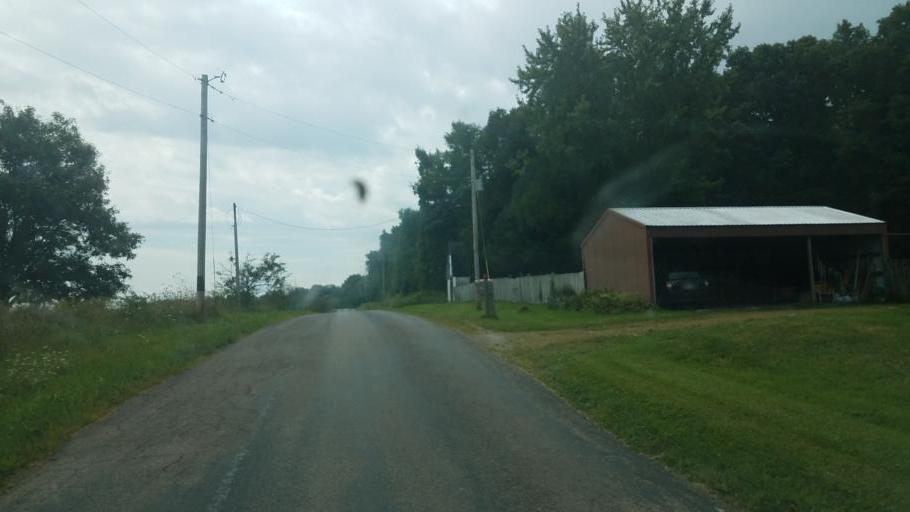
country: US
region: Ohio
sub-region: Ashland County
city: Loudonville
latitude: 40.5648
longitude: -82.3563
